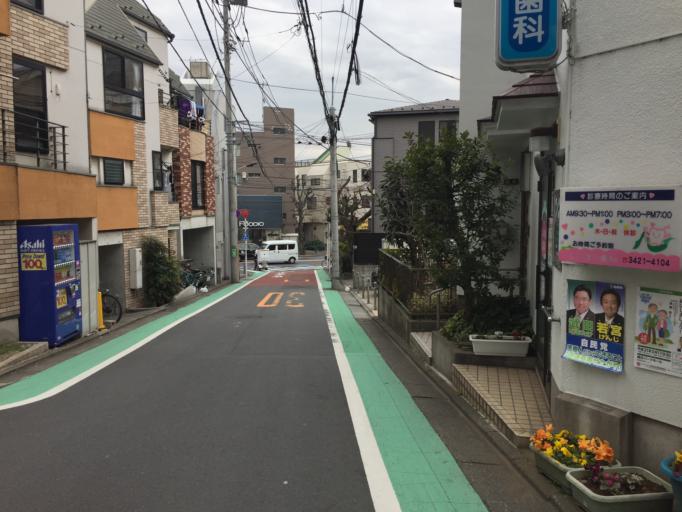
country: JP
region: Tokyo
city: Tokyo
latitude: 35.6552
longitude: 139.6733
